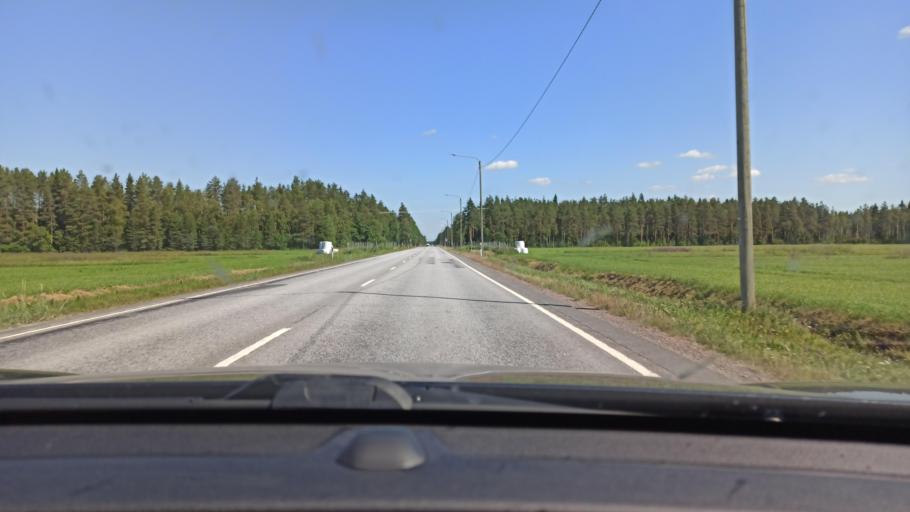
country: FI
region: Northern Ostrobothnia
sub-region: Raahe
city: Ruukki
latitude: 64.7222
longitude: 24.9956
